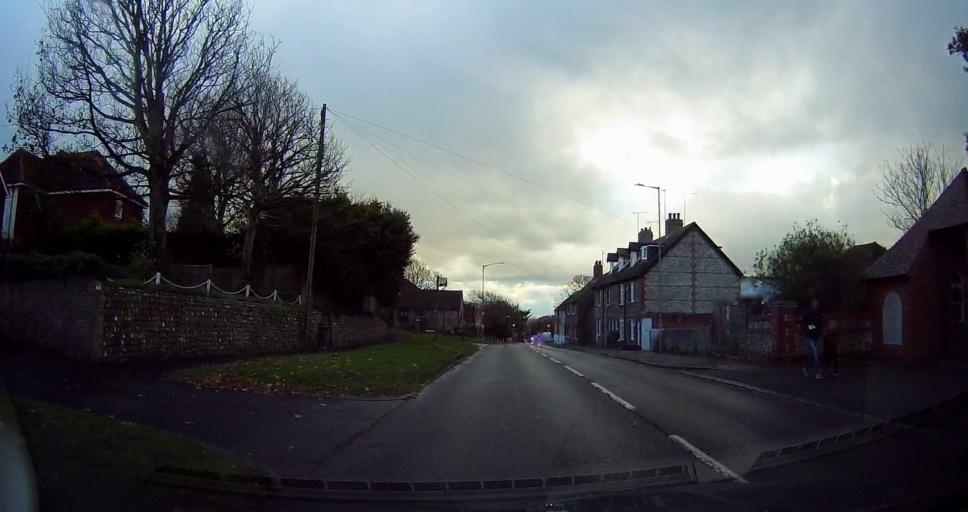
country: GB
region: England
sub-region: Brighton and Hove
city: Rottingdean
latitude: 50.8093
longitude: -0.0594
